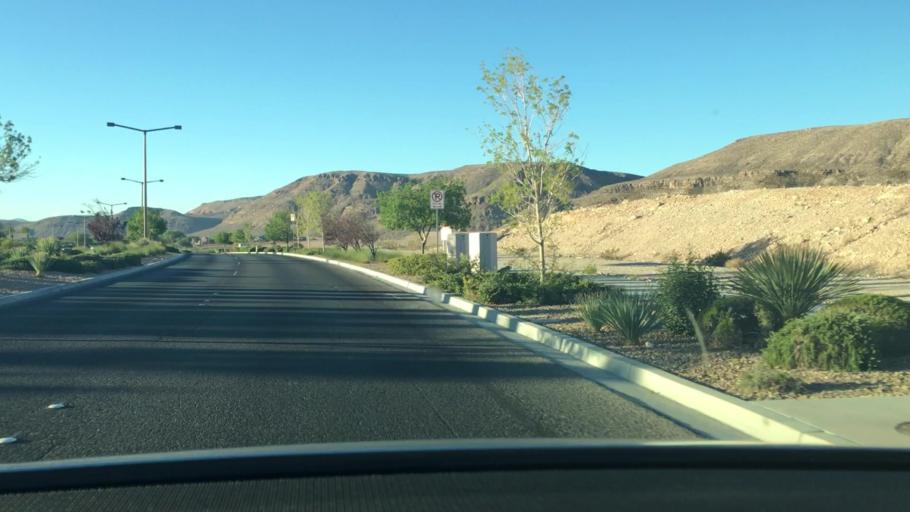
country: US
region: Nevada
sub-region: Clark County
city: Summerlin South
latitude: 36.0970
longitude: -115.3255
